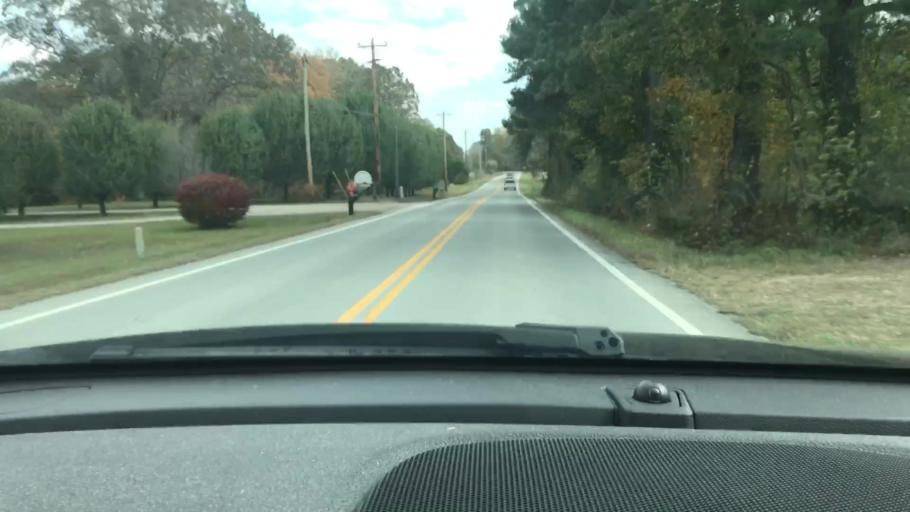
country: US
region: Tennessee
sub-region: Dickson County
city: Charlotte
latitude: 36.2133
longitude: -87.2679
